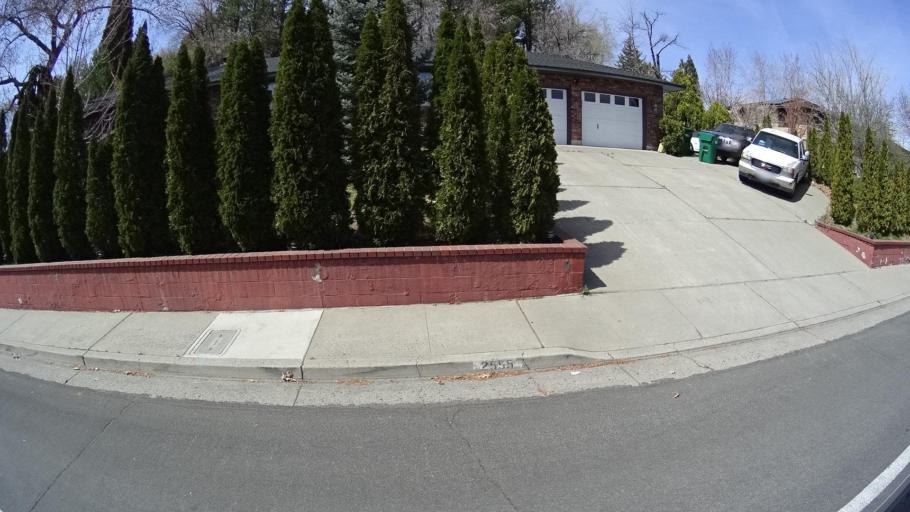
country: US
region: Nevada
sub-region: Washoe County
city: Reno
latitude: 39.5005
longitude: -119.8253
